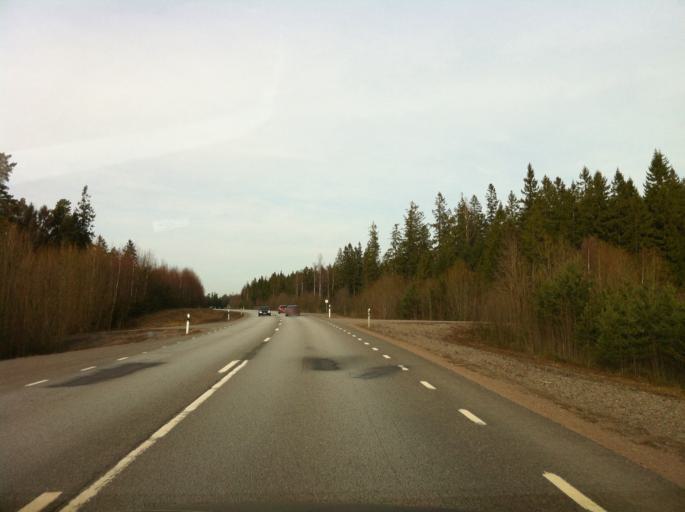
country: SE
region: Vaestra Goetaland
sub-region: Gullspangs Kommun
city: Gullspang
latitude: 58.8681
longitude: 14.0085
